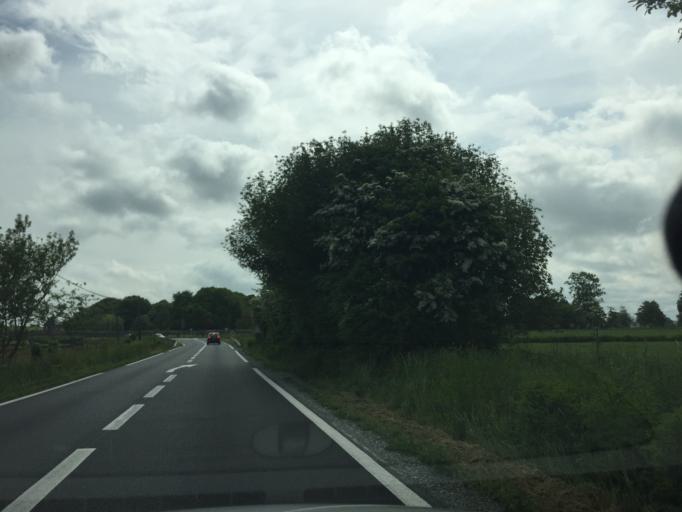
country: FR
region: Brittany
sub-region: Departement des Cotes-d'Armor
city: Crehen
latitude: 48.5654
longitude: -2.1920
